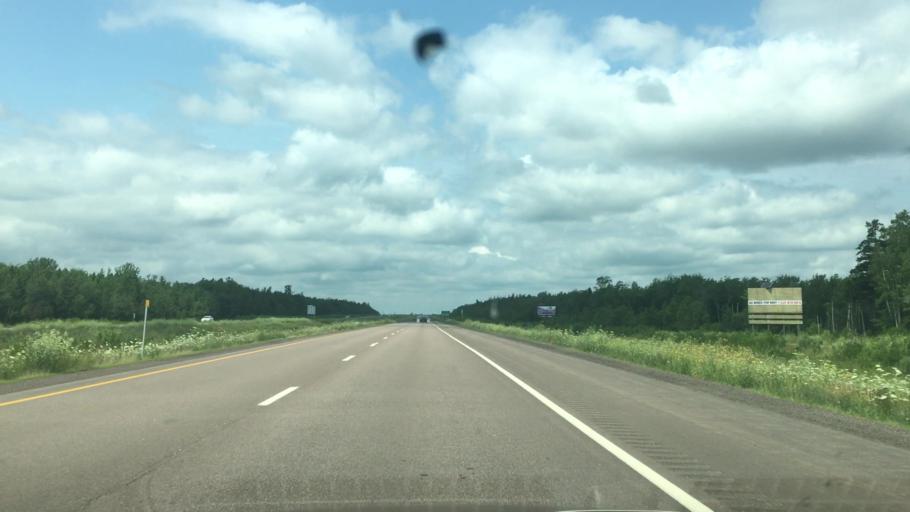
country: CA
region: New Brunswick
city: Dieppe
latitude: 46.1146
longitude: -64.6197
